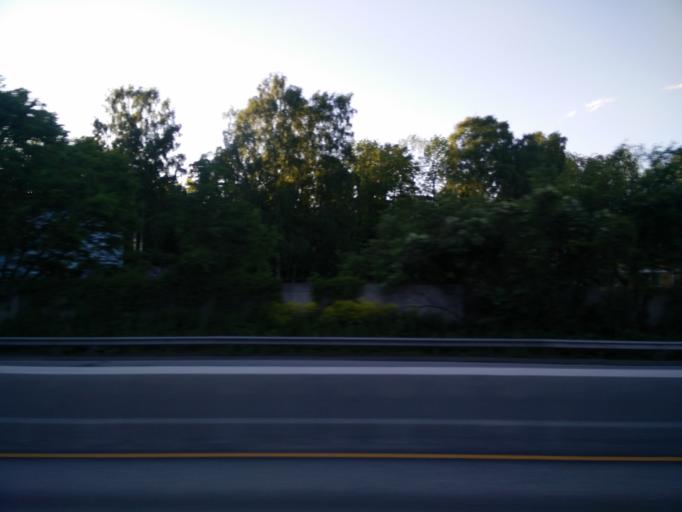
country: NO
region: Akershus
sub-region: Baerum
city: Lysaker
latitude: 59.9049
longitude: 10.6072
